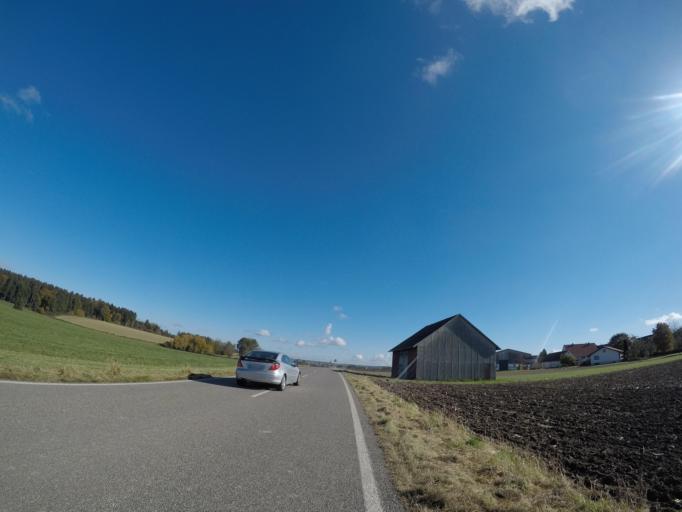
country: DE
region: Baden-Wuerttemberg
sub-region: Tuebingen Region
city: Durnau
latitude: 48.0785
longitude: 9.5728
